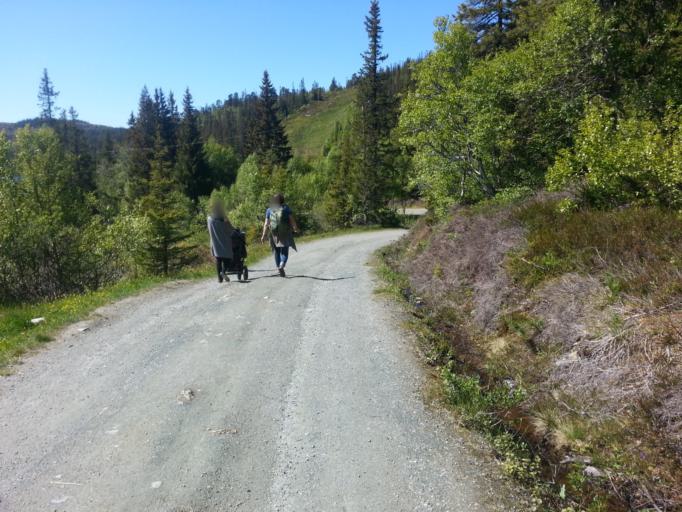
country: NO
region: Sor-Trondelag
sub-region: Melhus
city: Melhus
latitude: 63.4154
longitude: 10.2582
